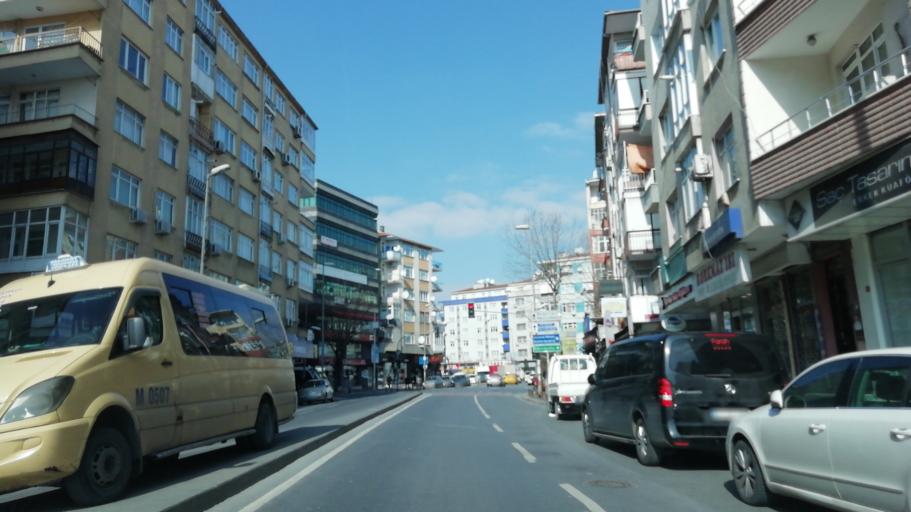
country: TR
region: Istanbul
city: Bahcelievler
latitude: 40.9950
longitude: 28.8489
